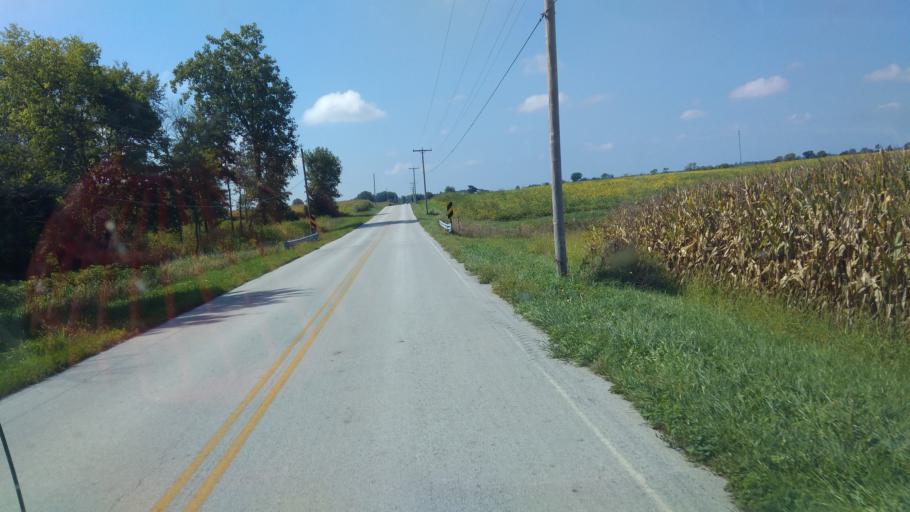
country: US
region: Ohio
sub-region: Hardin County
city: Kenton
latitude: 40.6666
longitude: -83.5909
